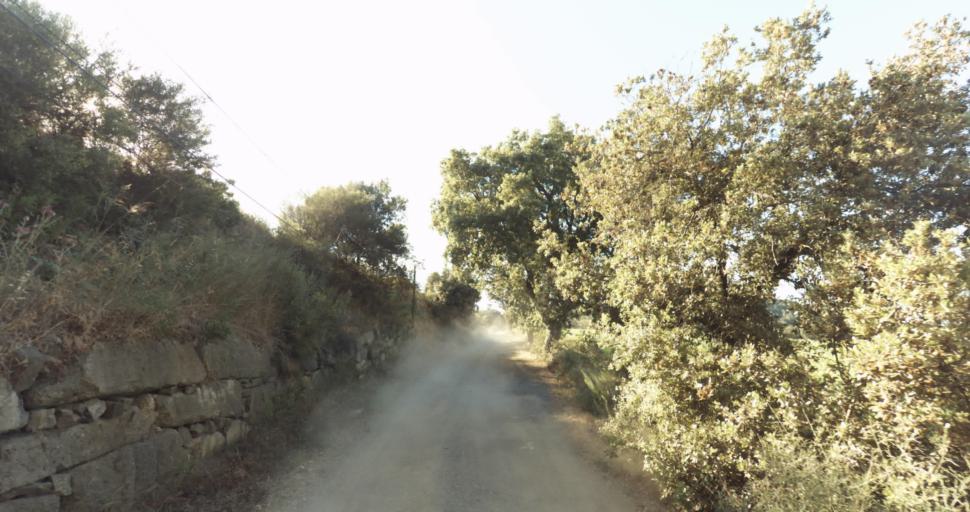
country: FR
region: Provence-Alpes-Cote d'Azur
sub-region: Departement du Var
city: La Croix-Valmer
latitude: 43.2188
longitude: 6.5638
